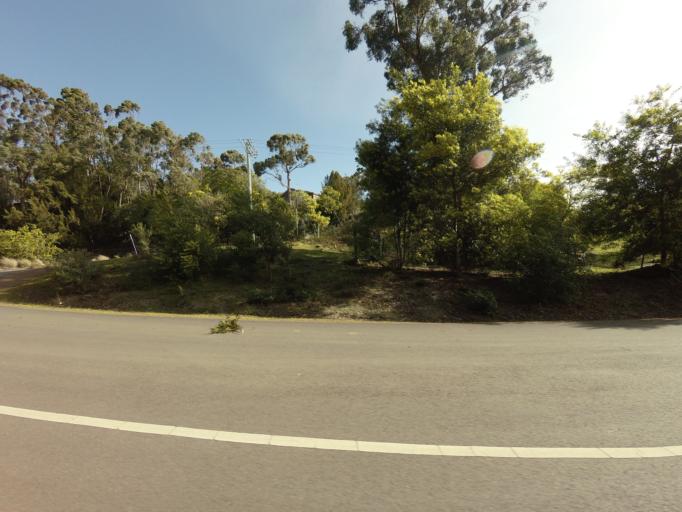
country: AU
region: Tasmania
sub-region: Kingborough
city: Margate
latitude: -43.0776
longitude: 147.2653
